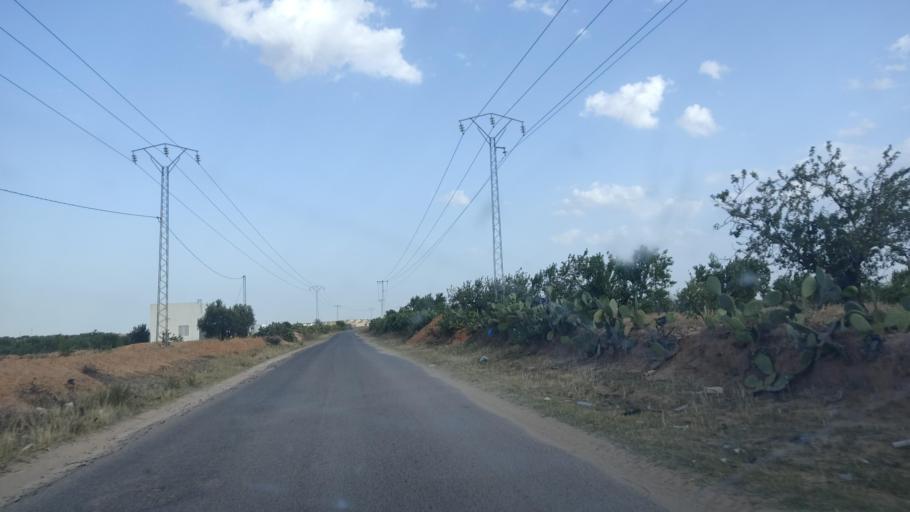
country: TN
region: Safaqis
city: Sfax
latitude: 34.8555
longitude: 10.6062
